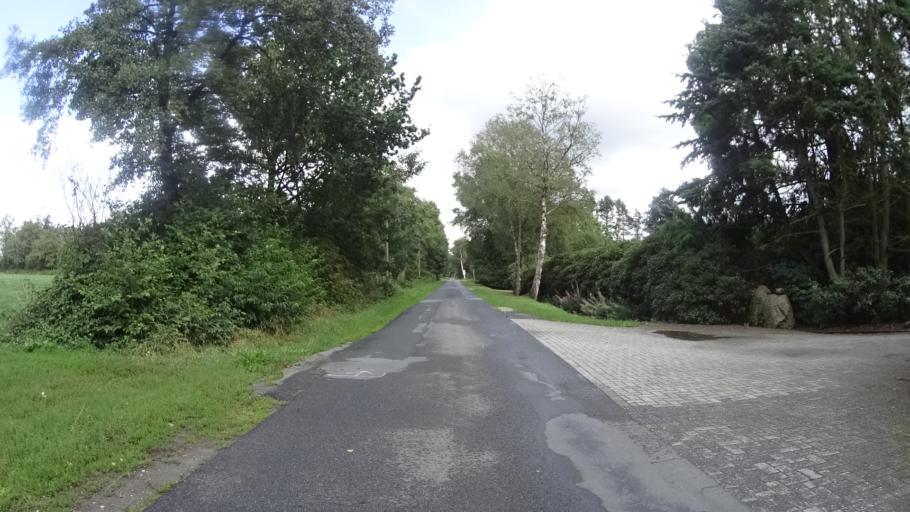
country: DE
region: Lower Saxony
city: Friedeburg
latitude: 53.3818
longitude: 7.8595
